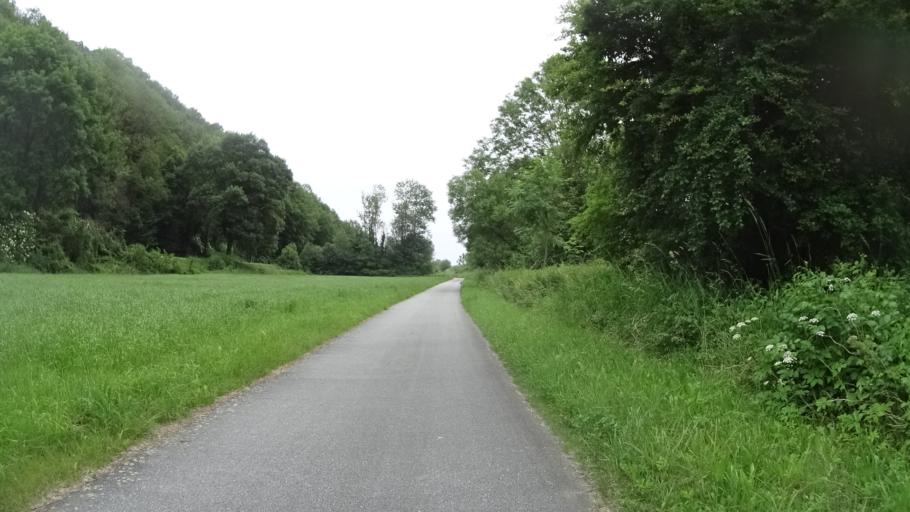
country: DE
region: Bavaria
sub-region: Lower Bavaria
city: Hofkirchen
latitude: 48.6588
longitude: 13.1533
